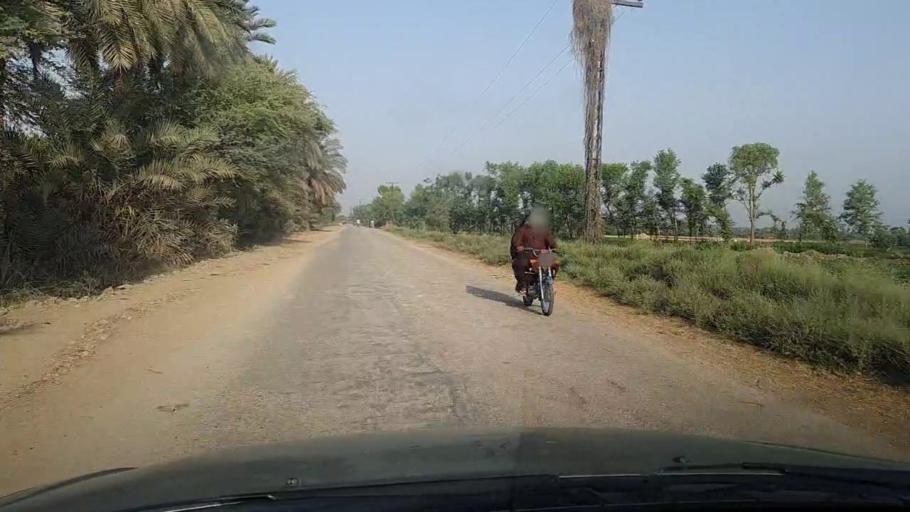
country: PK
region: Sindh
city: Pir jo Goth
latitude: 27.5714
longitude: 68.6000
